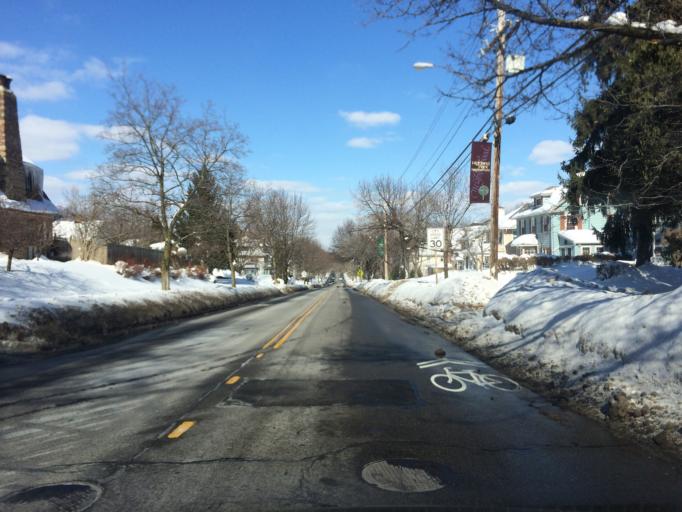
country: US
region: New York
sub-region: Monroe County
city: Rochester
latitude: 43.1335
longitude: -77.5996
